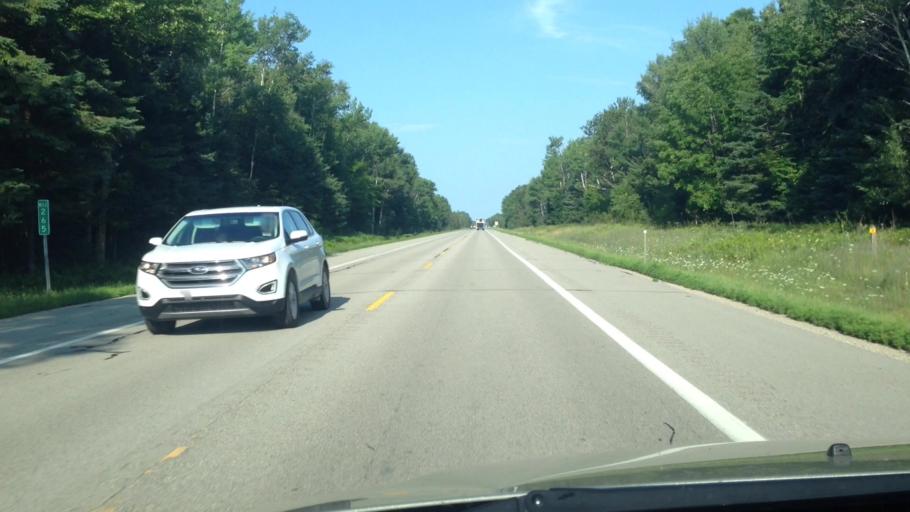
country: US
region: Michigan
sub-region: Luce County
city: Newberry
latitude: 46.1011
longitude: -85.7171
